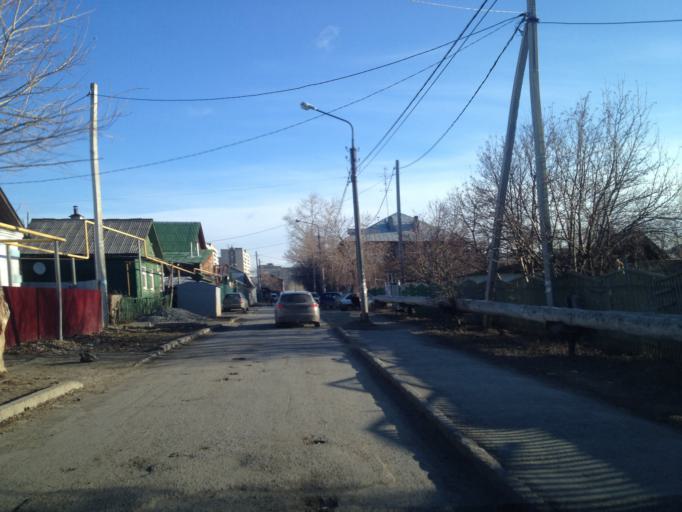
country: RU
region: Sverdlovsk
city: Sovkhoznyy
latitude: 56.7572
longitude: 60.6075
